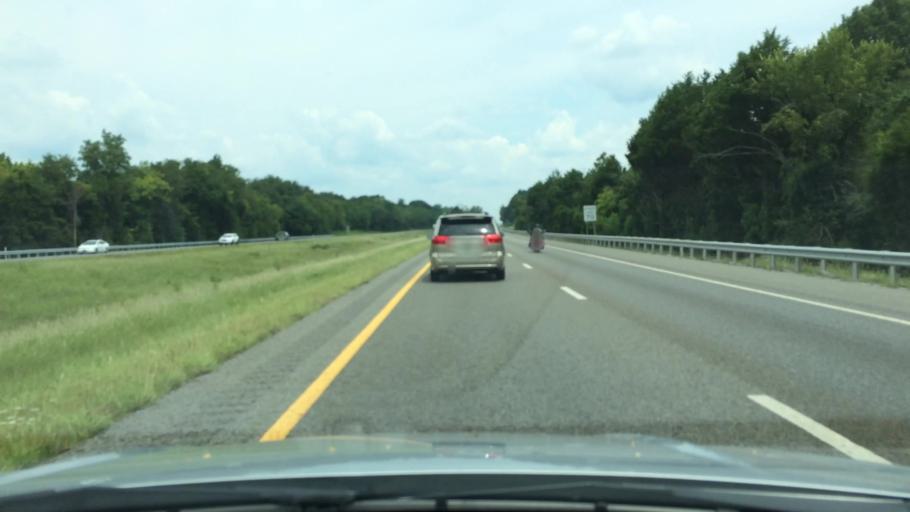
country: US
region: Tennessee
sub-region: Marshall County
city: Lewisburg
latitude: 35.4573
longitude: -86.8856
